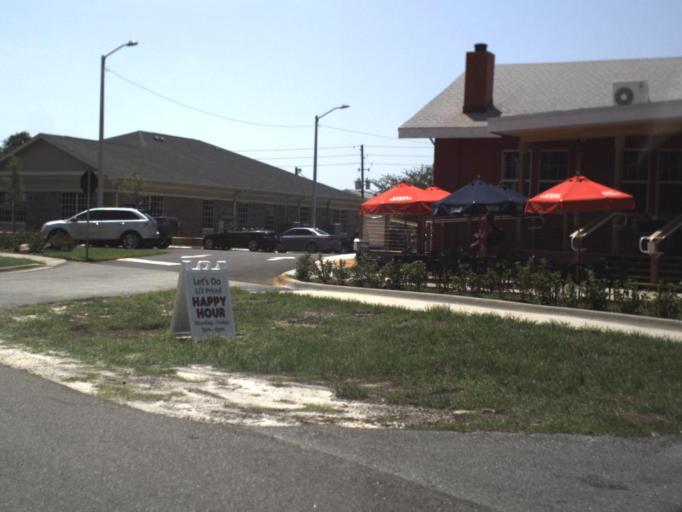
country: US
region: Florida
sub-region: Pinellas County
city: Palm Harbor
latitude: 28.1018
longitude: -82.7720
